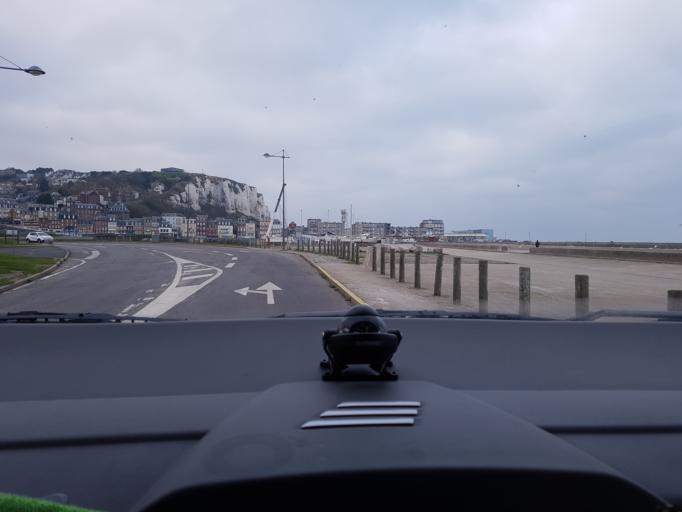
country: FR
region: Haute-Normandie
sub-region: Departement de la Seine-Maritime
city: Le Treport
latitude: 50.0632
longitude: 1.3759
